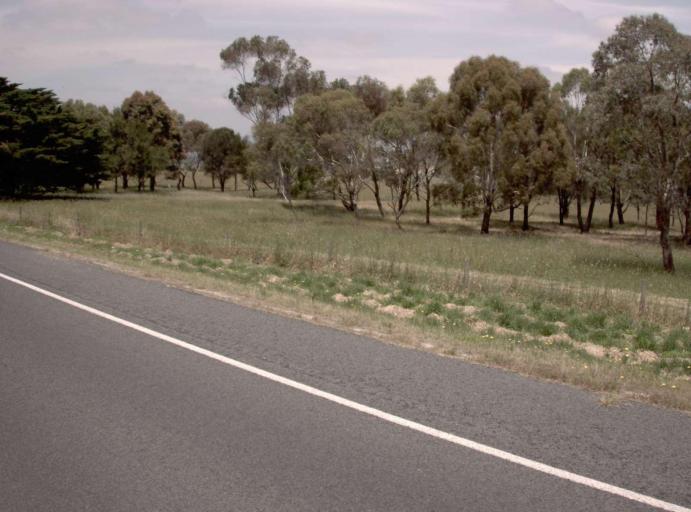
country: AU
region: Victoria
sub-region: Latrobe
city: Traralgon
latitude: -38.2326
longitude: 146.5407
